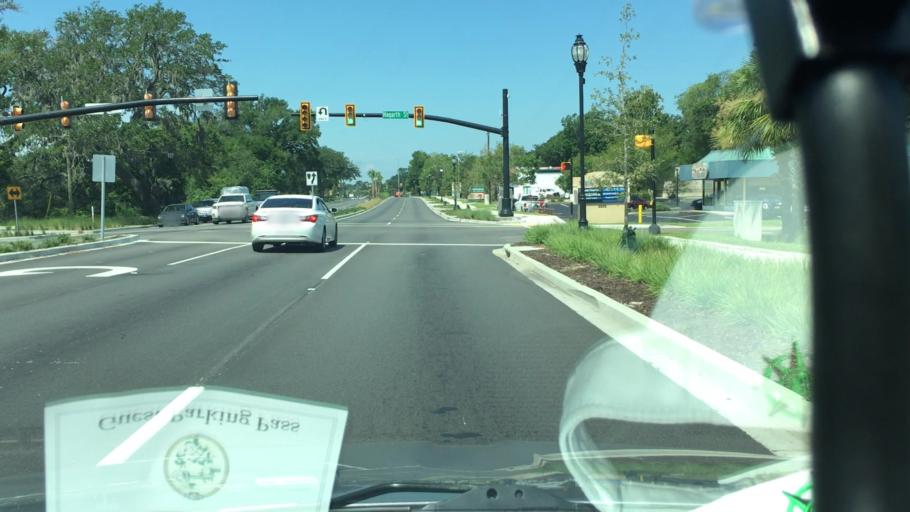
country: US
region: South Carolina
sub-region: Beaufort County
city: Burton
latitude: 32.4414
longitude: -80.6989
